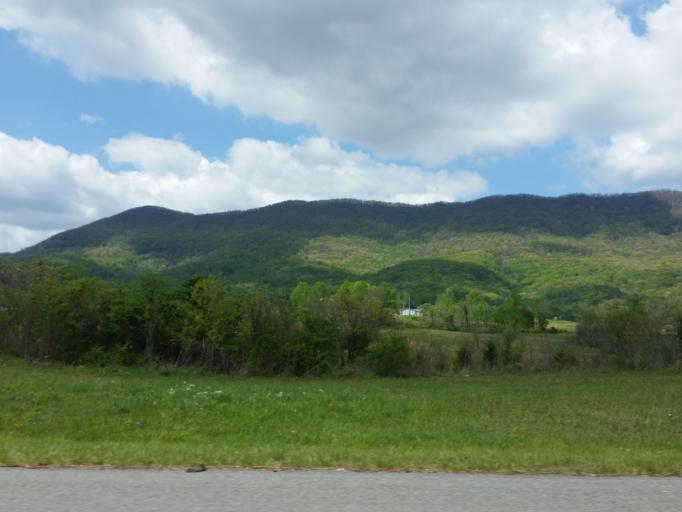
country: US
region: Tennessee
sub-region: Campbell County
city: Fincastle
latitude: 36.4472
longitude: -83.9375
